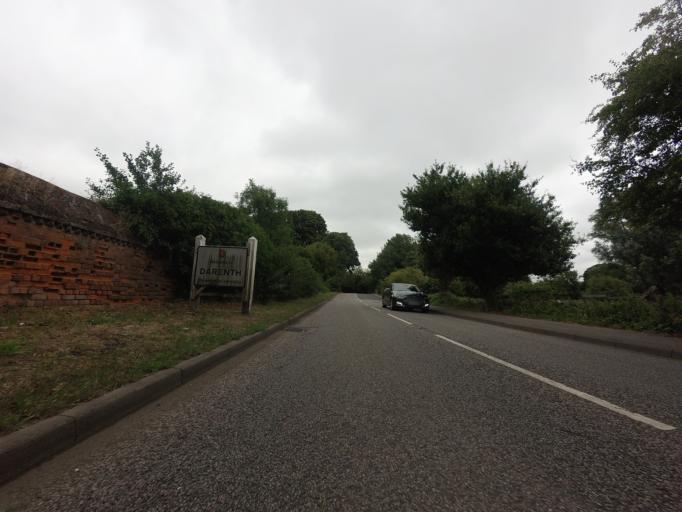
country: GB
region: England
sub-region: Kent
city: Dartford
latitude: 51.4171
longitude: 0.2376
